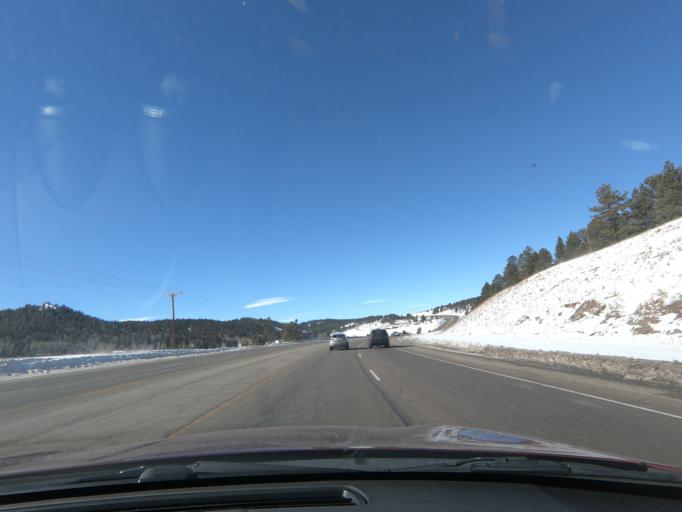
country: US
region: Colorado
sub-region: Teller County
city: Woodland Park
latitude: 38.9573
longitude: -105.1001
